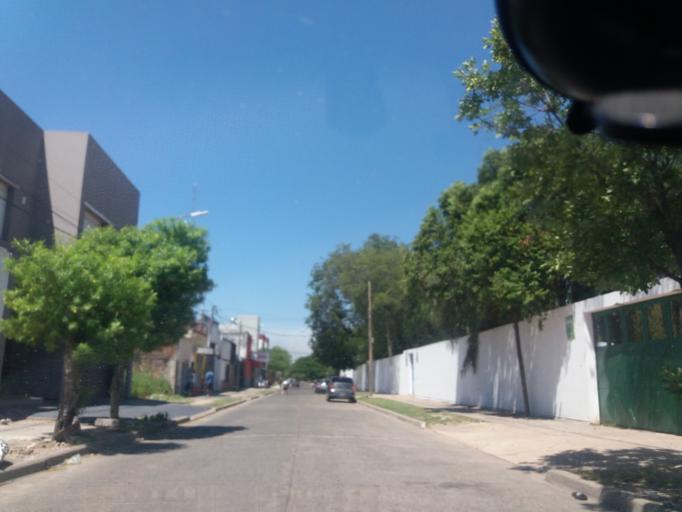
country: AR
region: Corrientes
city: Corrientes
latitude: -27.4833
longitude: -58.8455
